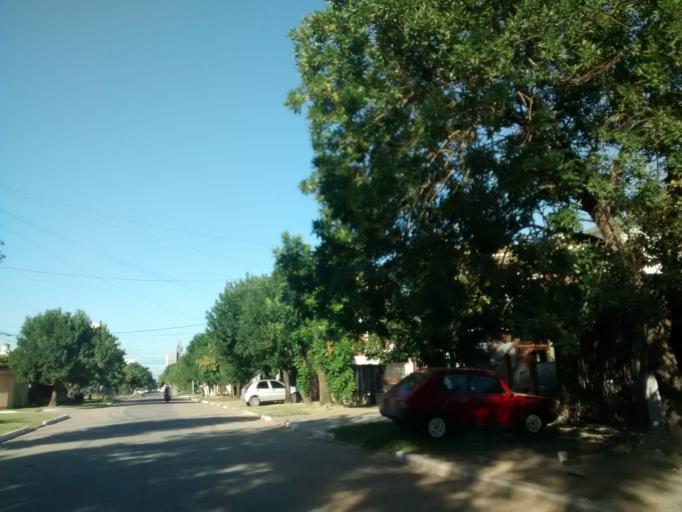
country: AR
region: Chaco
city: Resistencia
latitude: -27.4596
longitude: -58.9994
